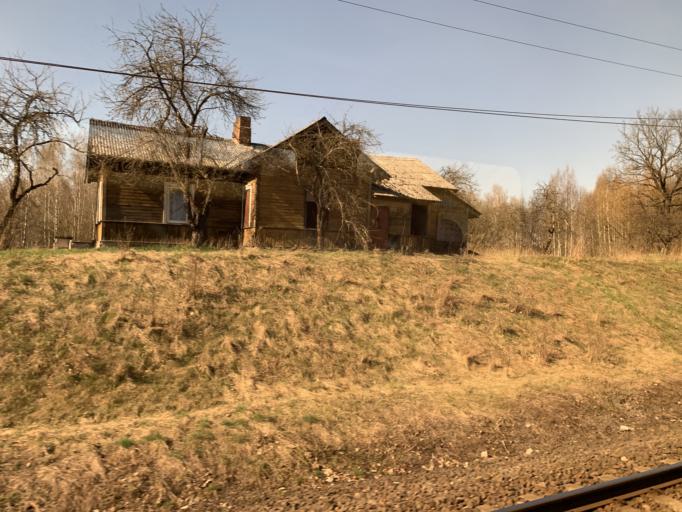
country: LT
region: Vilnius County
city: Rasos
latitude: 54.6826
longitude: 25.3666
